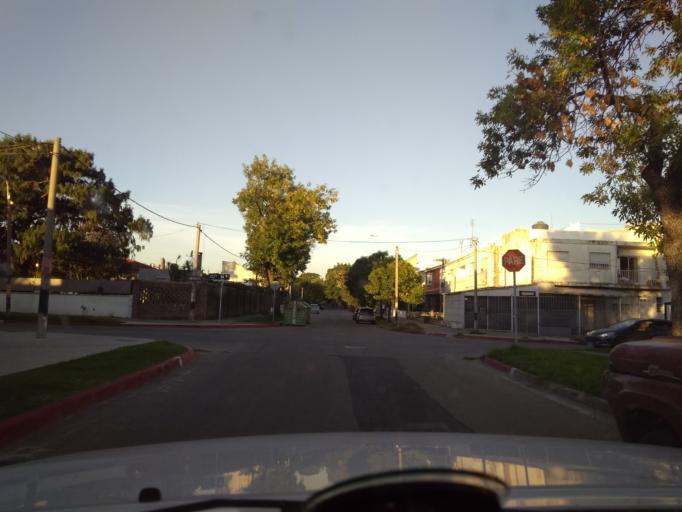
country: UY
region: Montevideo
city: Montevideo
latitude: -34.8907
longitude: -56.1441
